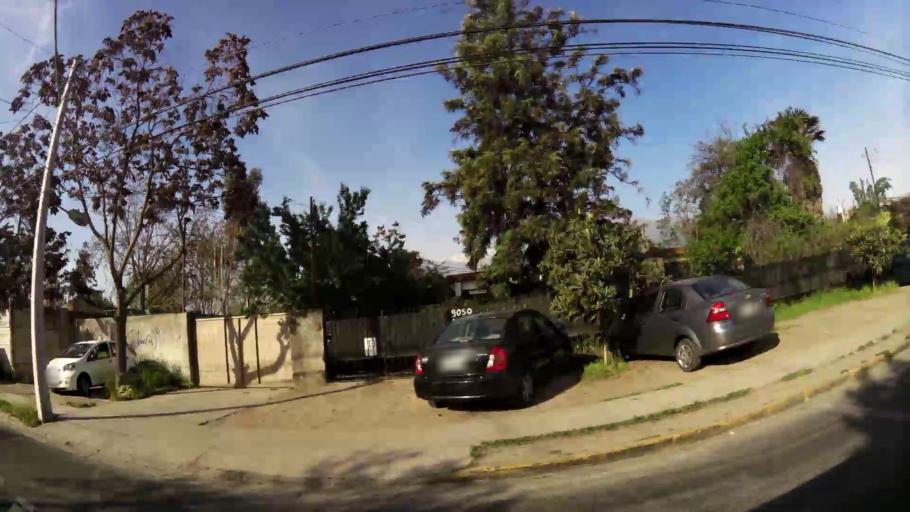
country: CL
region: Santiago Metropolitan
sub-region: Provincia de Santiago
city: La Pintana
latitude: -33.5375
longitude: -70.5867
